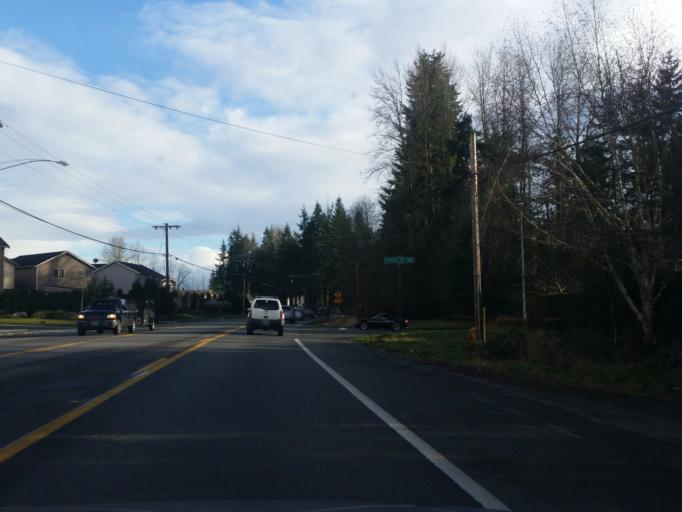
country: US
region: Washington
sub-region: Snohomish County
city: Martha Lake
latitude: 47.8226
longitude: -122.2352
